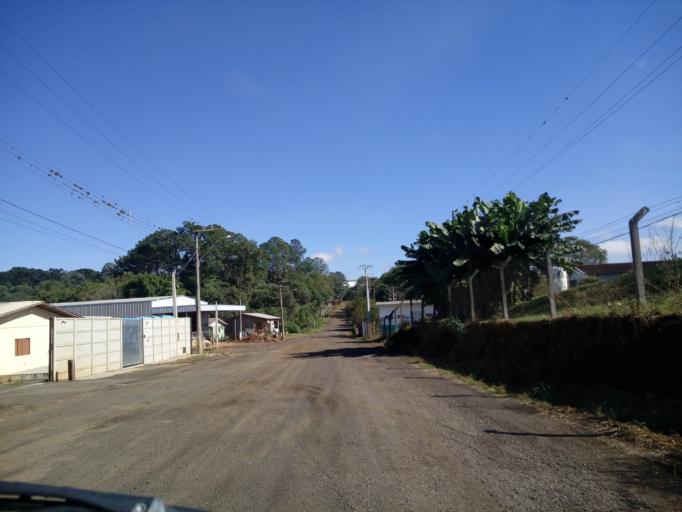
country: BR
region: Santa Catarina
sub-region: Chapeco
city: Chapeco
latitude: -27.0965
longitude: -52.6555
